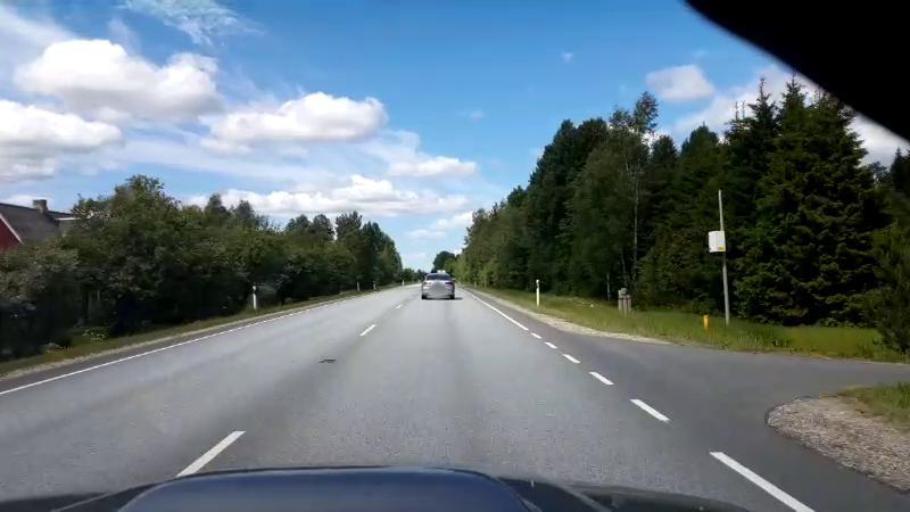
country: EE
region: Paernumaa
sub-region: Halinga vald
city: Parnu-Jaagupi
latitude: 58.5548
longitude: 24.5289
